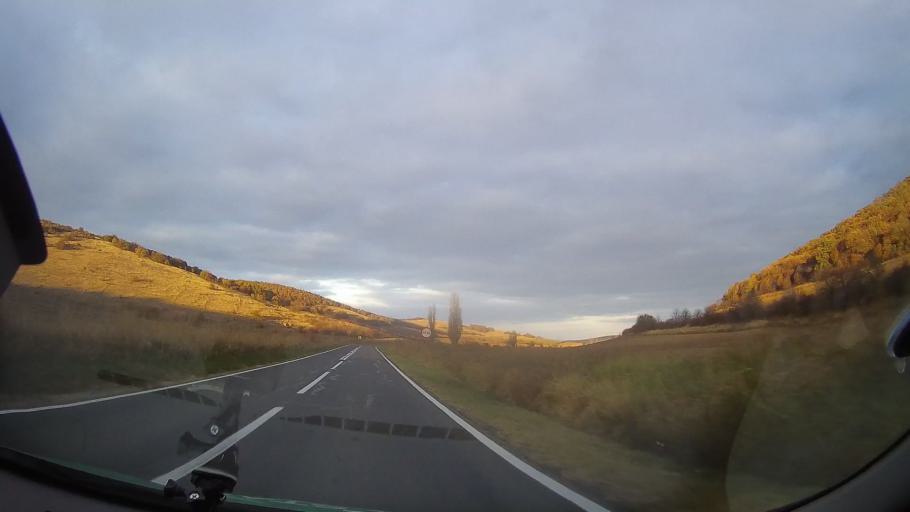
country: RO
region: Tulcea
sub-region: Comuna Ciucurova
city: Ciucurova
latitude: 44.9601
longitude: 28.5192
